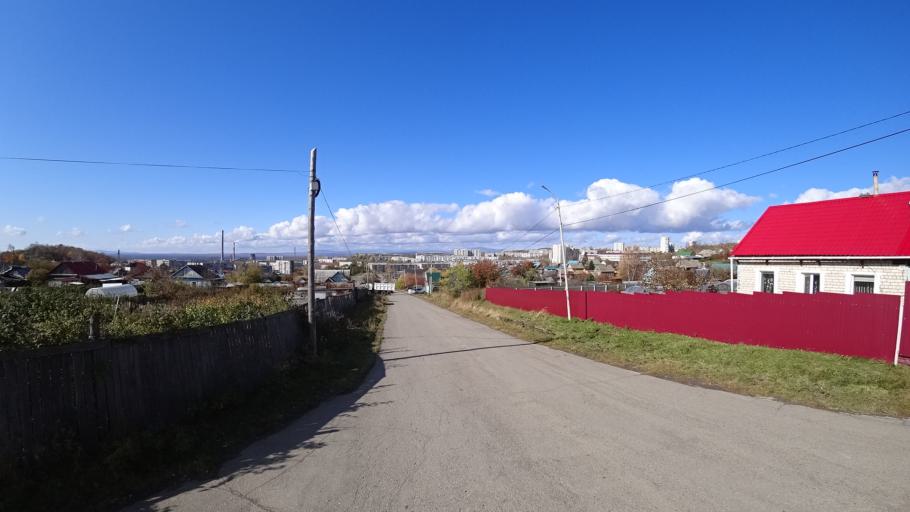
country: RU
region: Khabarovsk Krai
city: Amursk
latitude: 50.2353
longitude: 136.9225
